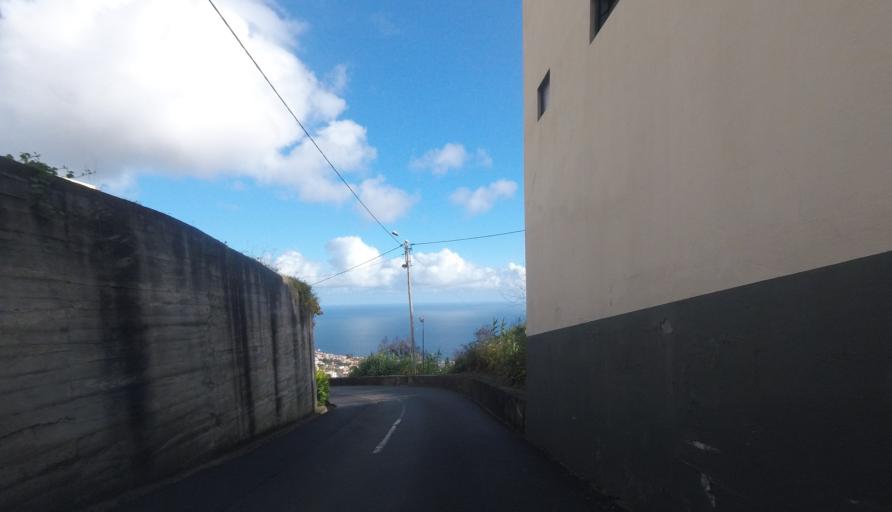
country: PT
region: Madeira
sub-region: Funchal
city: Nossa Senhora do Monte
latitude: 32.6679
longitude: -16.9025
